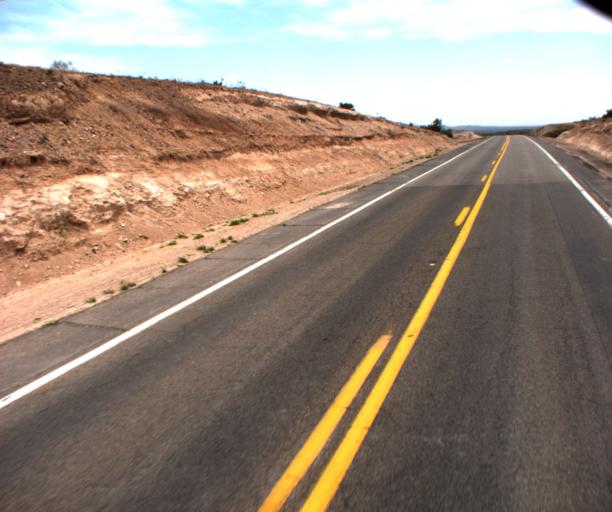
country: US
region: Arizona
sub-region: Graham County
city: Bylas
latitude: 33.2136
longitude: -110.2105
